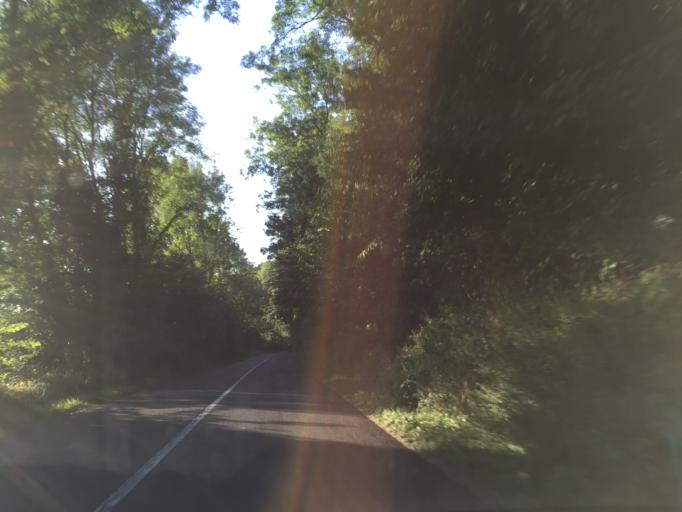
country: FR
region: Lower Normandy
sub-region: Departement du Calvados
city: Equemauville
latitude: 49.4010
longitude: 0.1820
